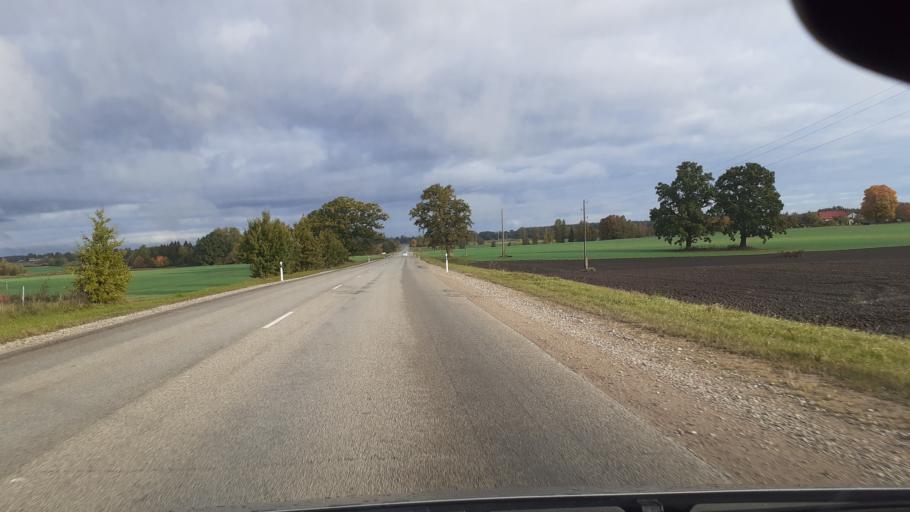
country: LV
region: Kuldigas Rajons
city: Kuldiga
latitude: 56.9733
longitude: 21.9321
